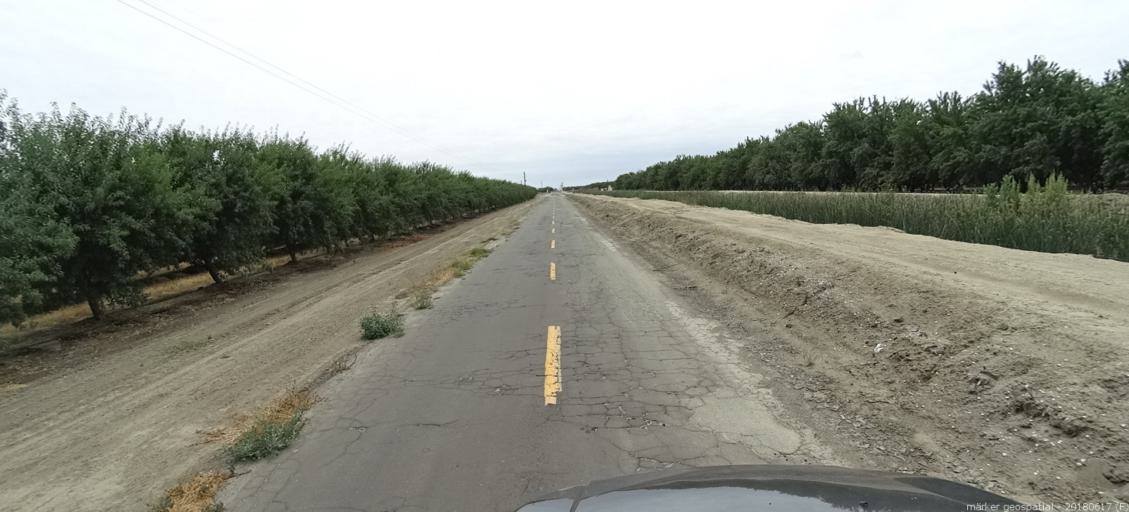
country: US
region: California
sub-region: Madera County
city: Fairmead
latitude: 36.9820
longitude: -120.2232
